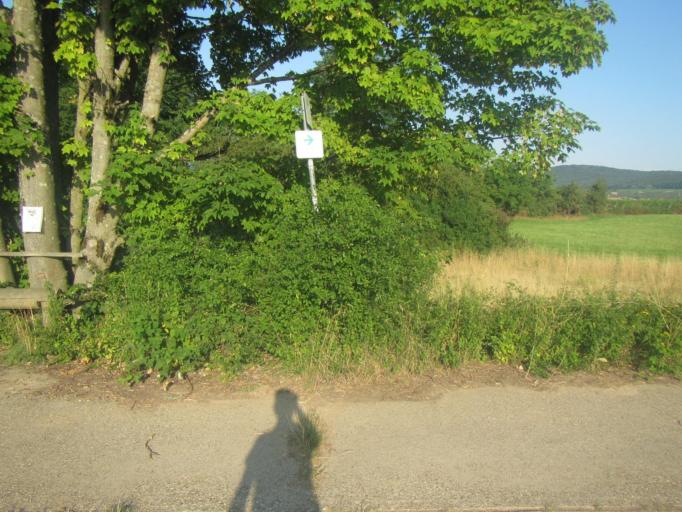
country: DE
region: Rheinland-Pfalz
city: Schweigen-Rechtenbach
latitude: 49.0457
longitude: 7.9744
